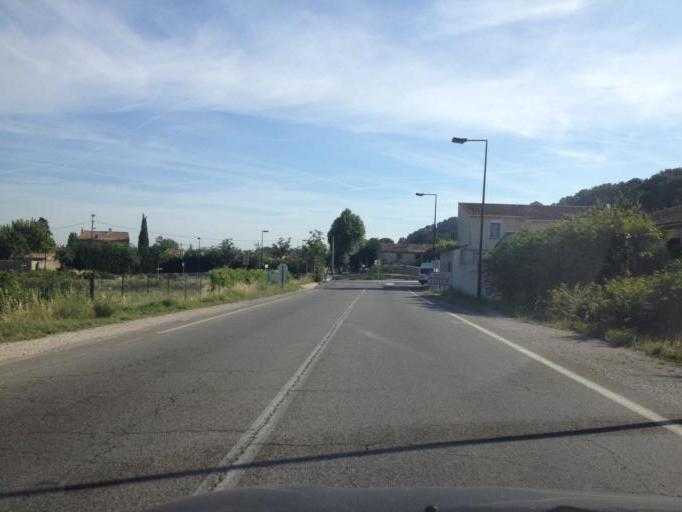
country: FR
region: Provence-Alpes-Cote d'Azur
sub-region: Departement du Vaucluse
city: Orange
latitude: 44.1251
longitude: 4.8006
